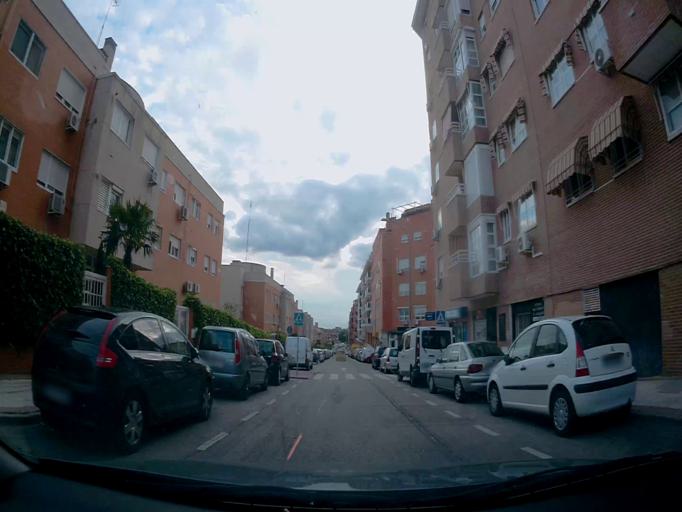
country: ES
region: Madrid
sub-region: Provincia de Madrid
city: Alcorcon
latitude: 40.3373
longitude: -3.8265
